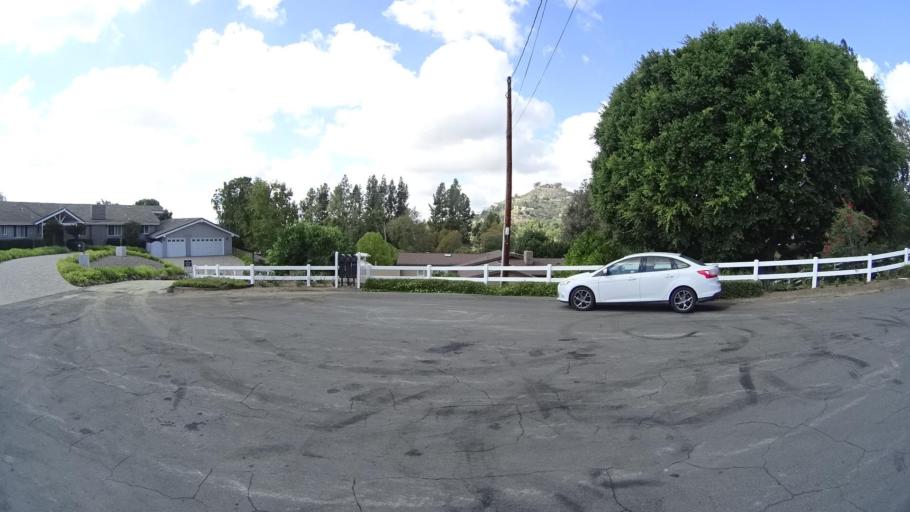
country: US
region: California
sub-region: San Diego County
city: Casa de Oro-Mount Helix
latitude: 32.7639
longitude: -116.9676
